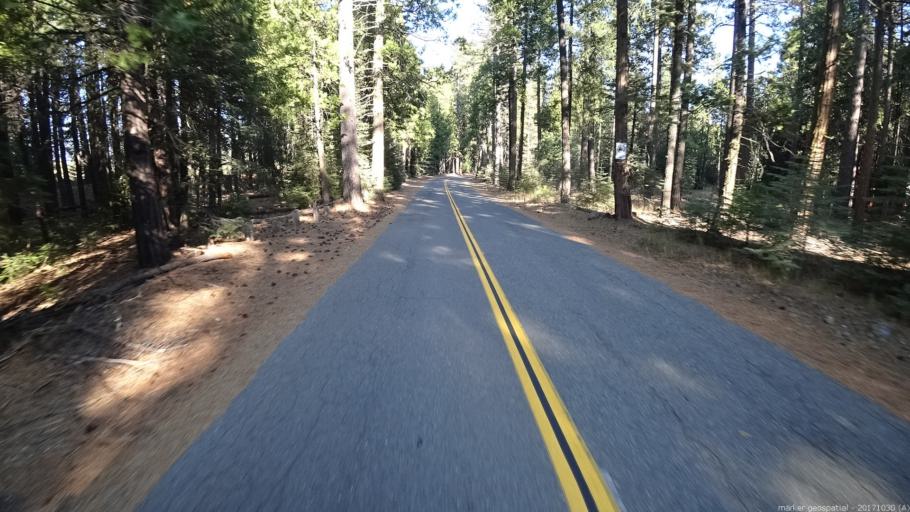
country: US
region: California
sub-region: Shasta County
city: Shingletown
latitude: 40.5366
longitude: -121.7348
